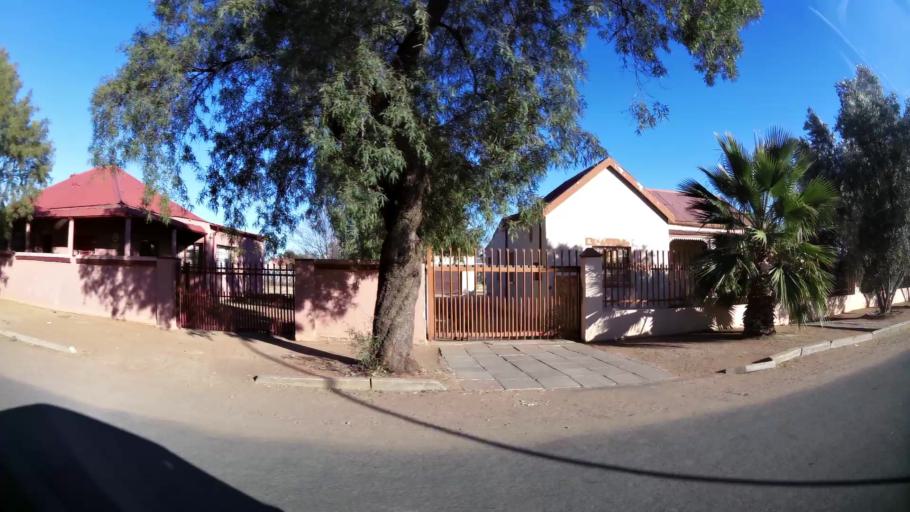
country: ZA
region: Northern Cape
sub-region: Frances Baard District Municipality
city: Kimberley
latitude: -28.7370
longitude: 24.7435
